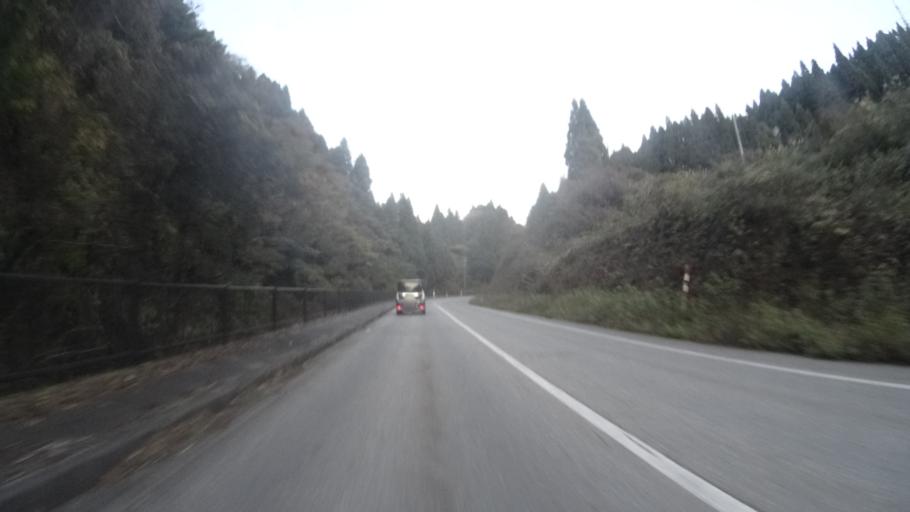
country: JP
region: Ishikawa
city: Nanao
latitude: 37.3221
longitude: 136.8128
